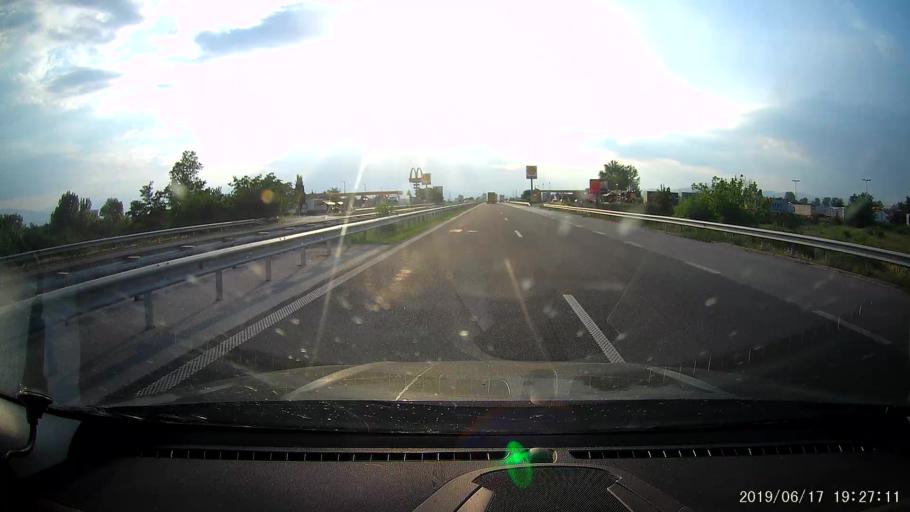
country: BG
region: Pazardzhik
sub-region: Obshtina Pazardzhik
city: Pazardzhik
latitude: 42.2640
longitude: 24.3100
